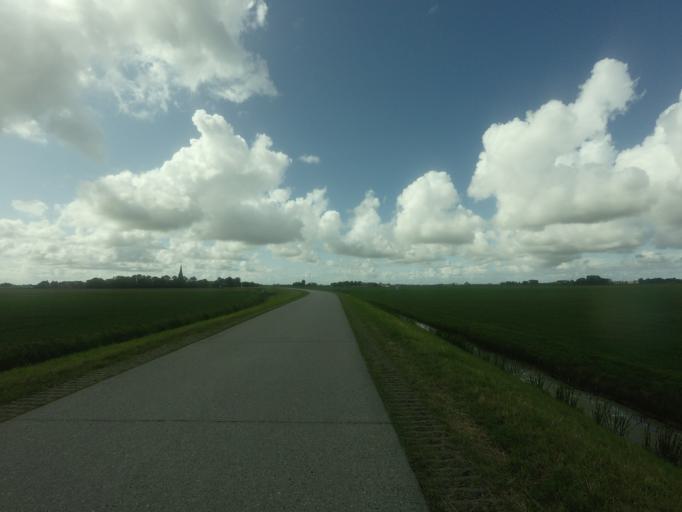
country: NL
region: Friesland
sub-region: Sudwest Fryslan
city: Scharnegoutum
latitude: 53.0780
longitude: 5.6443
